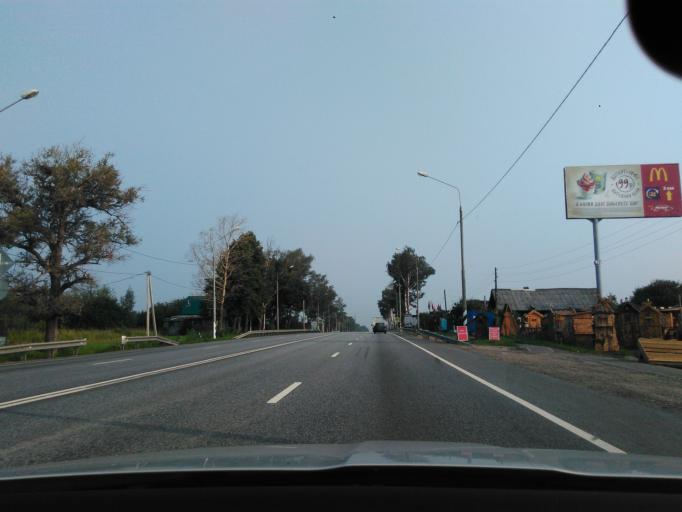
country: RU
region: Tverskaya
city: Zavidovo
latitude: 56.5504
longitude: 36.5148
